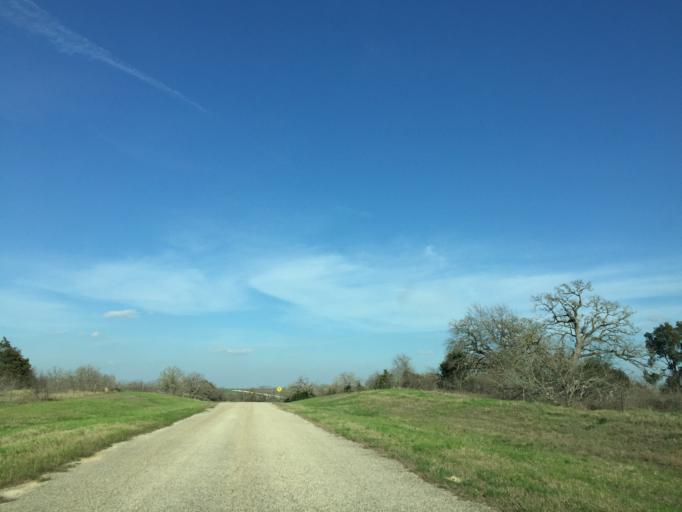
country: US
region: Texas
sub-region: Lee County
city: Lexington
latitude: 30.4552
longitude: -97.1604
